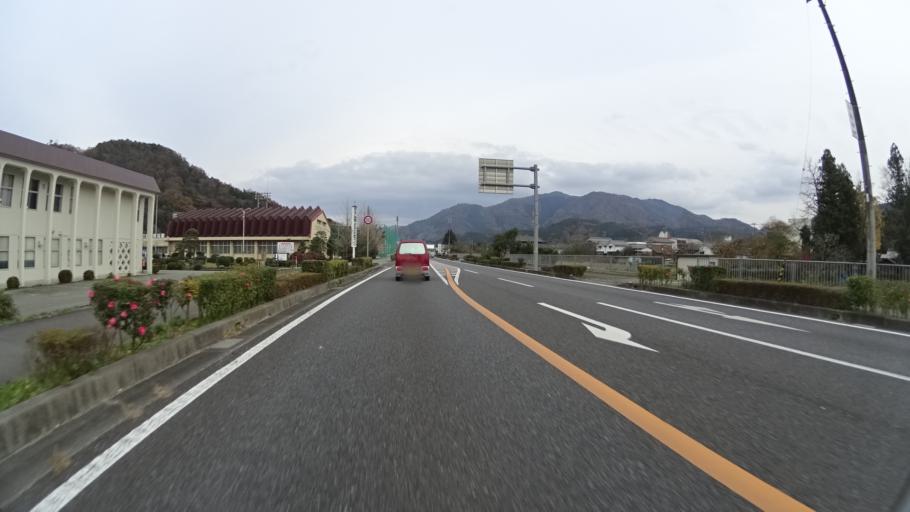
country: JP
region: Hyogo
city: Sasayama
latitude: 35.0700
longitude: 135.2790
